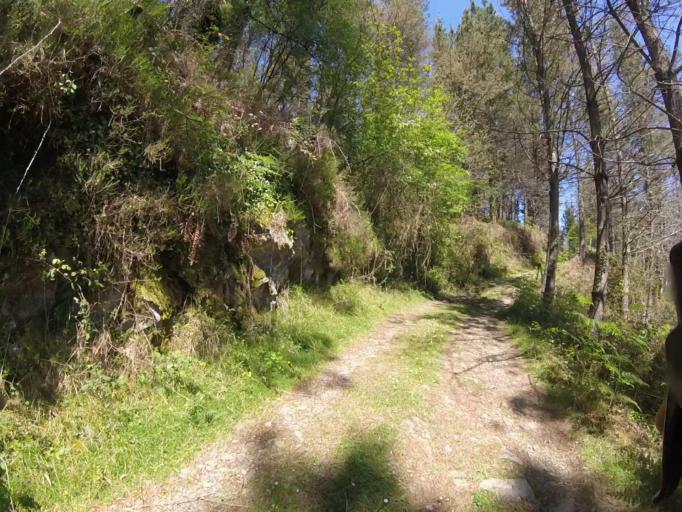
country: ES
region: Navarre
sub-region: Provincia de Navarra
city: Lesaka
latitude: 43.2489
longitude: -1.7567
